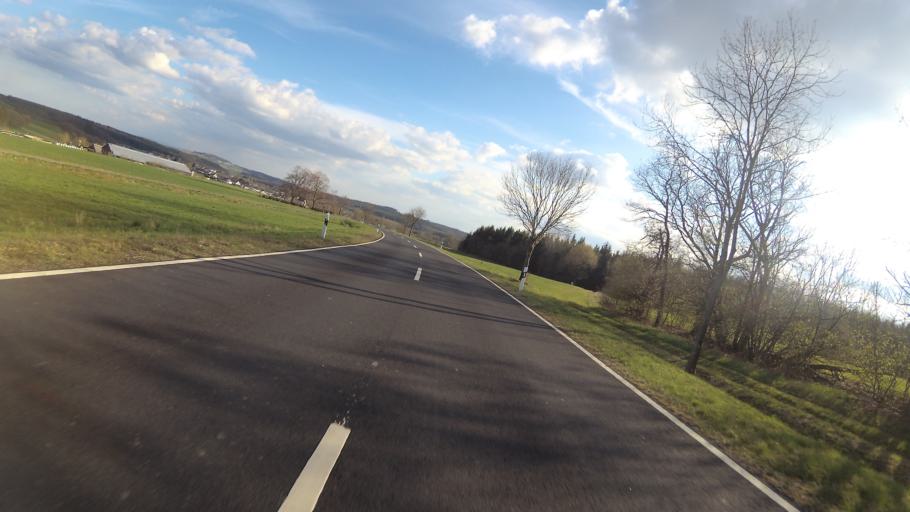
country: DE
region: Rheinland-Pfalz
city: Darscheid
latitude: 50.2232
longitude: 6.8818
